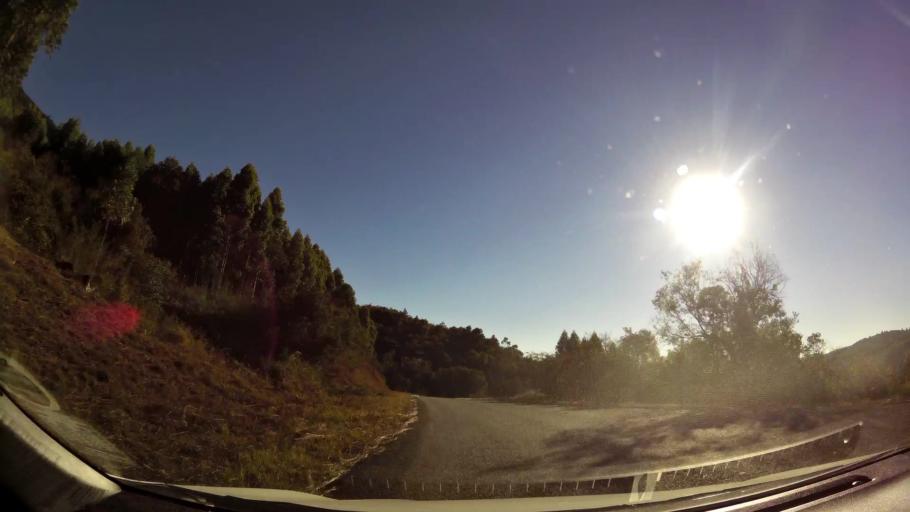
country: ZA
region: Limpopo
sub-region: Mopani District Municipality
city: Tzaneen
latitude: -23.9524
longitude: 30.0127
